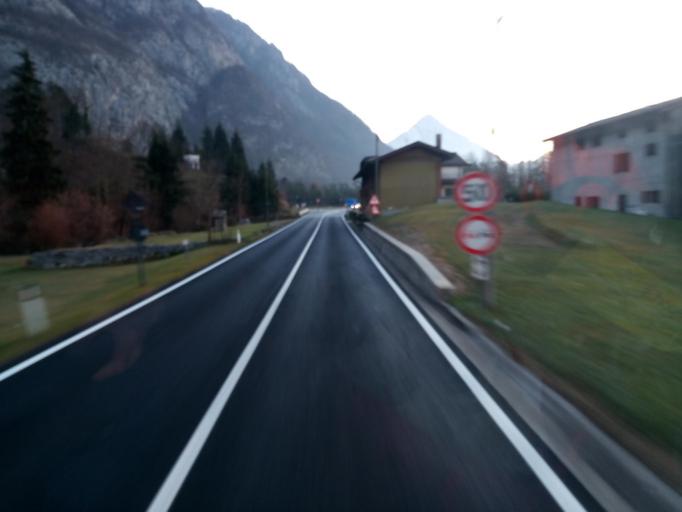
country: IT
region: Friuli Venezia Giulia
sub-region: Provincia di Udine
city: Lauco
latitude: 46.4109
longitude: 12.9572
